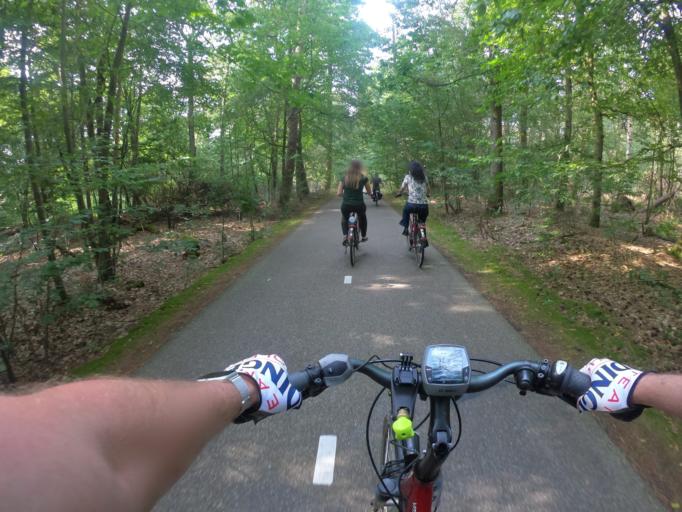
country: NL
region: Gelderland
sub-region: Gemeente Nijmegen
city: Nijmegen
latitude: 51.8032
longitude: 5.8585
